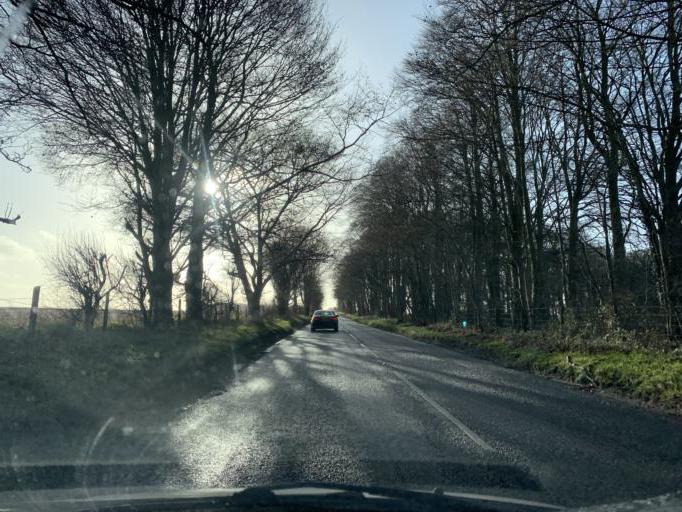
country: GB
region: England
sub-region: Wiltshire
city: Winterbourne Stoke
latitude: 51.1595
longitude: -1.8591
